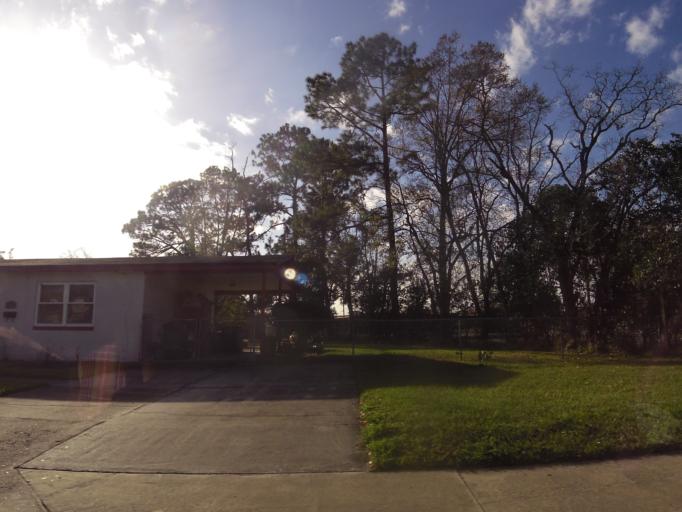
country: US
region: Florida
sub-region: Duval County
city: Jacksonville
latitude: 30.2769
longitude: -81.6100
